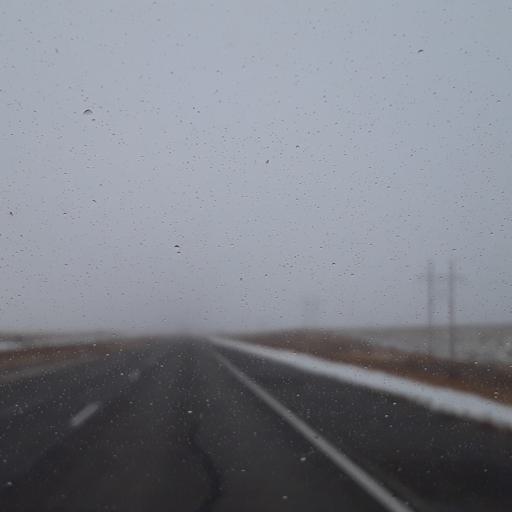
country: US
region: Colorado
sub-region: Logan County
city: Sterling
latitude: 40.7770
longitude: -102.9229
